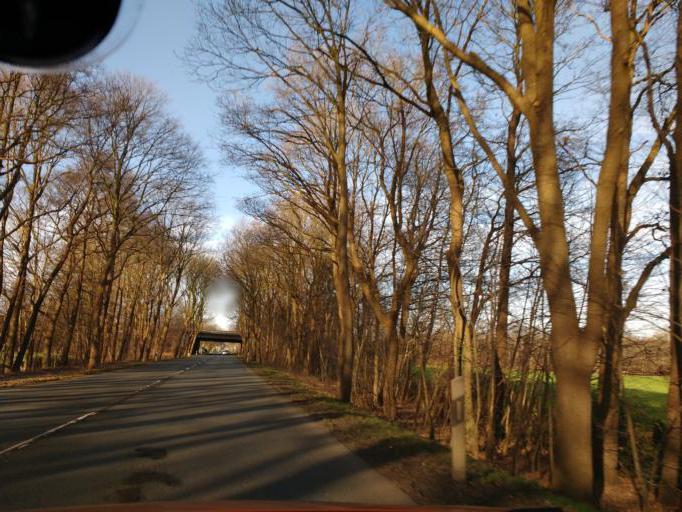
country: DE
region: Lower Saxony
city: Oldenburg
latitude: 53.1081
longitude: 8.2739
